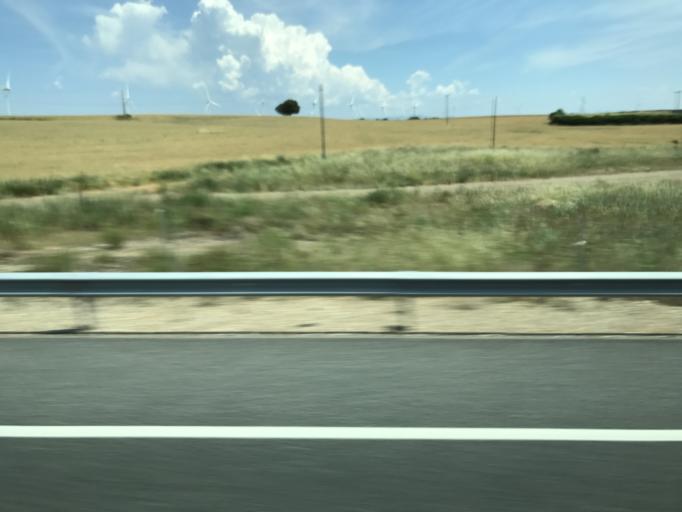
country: ES
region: Castille and Leon
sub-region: Provincia de Burgos
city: Cogollos
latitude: 42.2121
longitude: -3.7020
